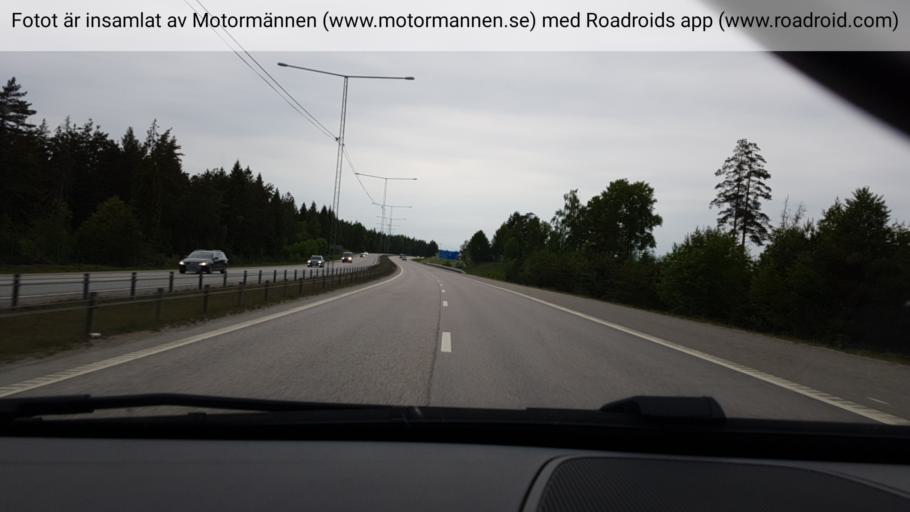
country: SE
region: Stockholm
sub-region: Haninge Kommun
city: Haninge
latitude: 59.1446
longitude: 18.1613
